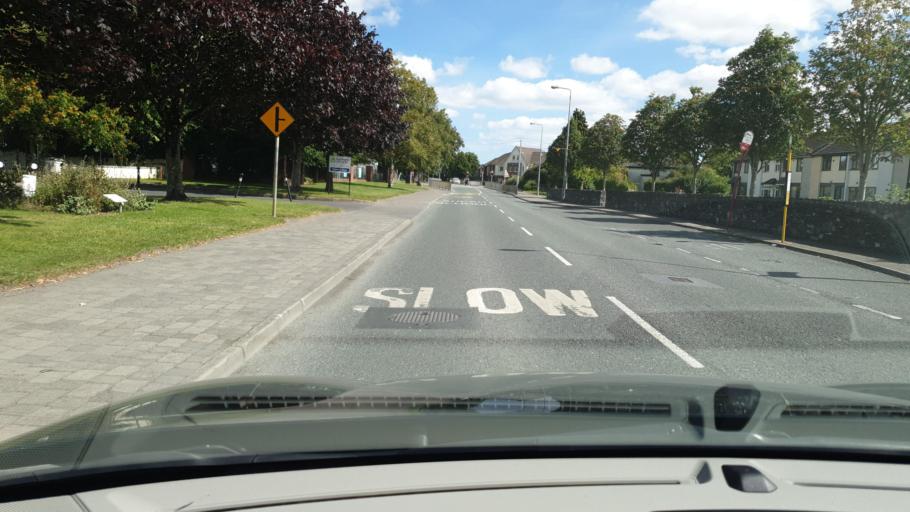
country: IE
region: Leinster
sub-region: An Mhi
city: Dunboyne
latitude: 53.4185
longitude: -6.4731
